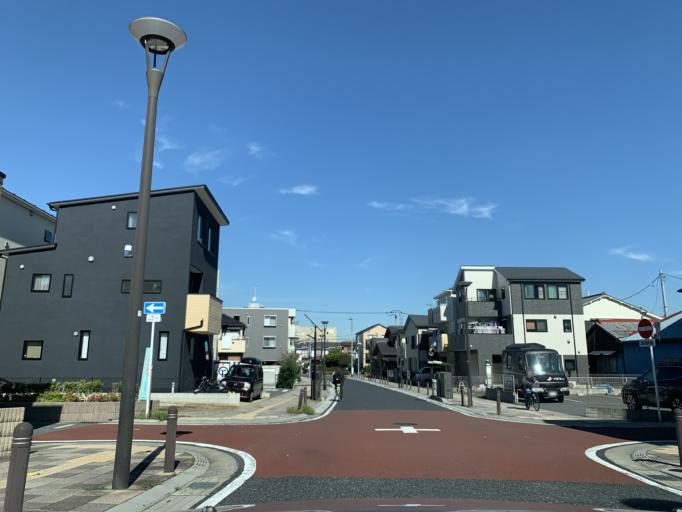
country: JP
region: Tokyo
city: Urayasu
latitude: 35.6612
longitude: 139.8949
